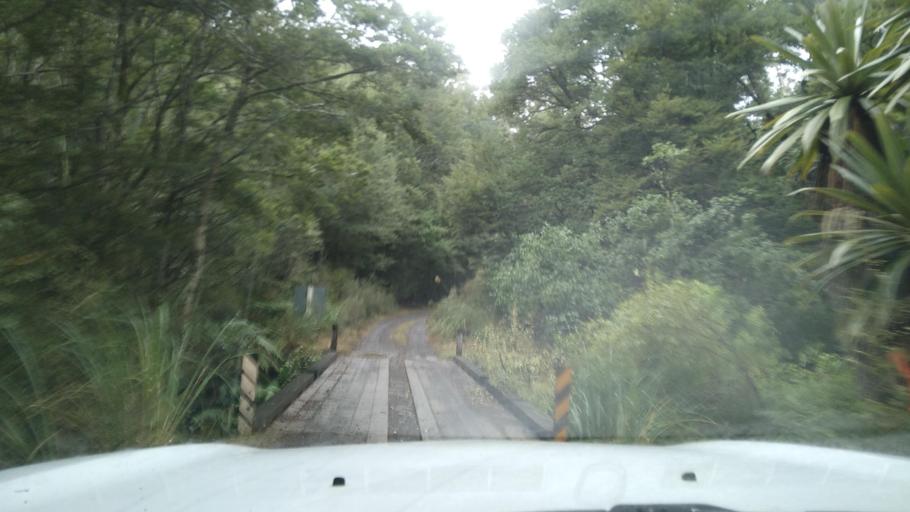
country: NZ
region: Manawatu-Wanganui
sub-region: Ruapehu District
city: Waiouru
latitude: -39.4123
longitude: 175.5006
